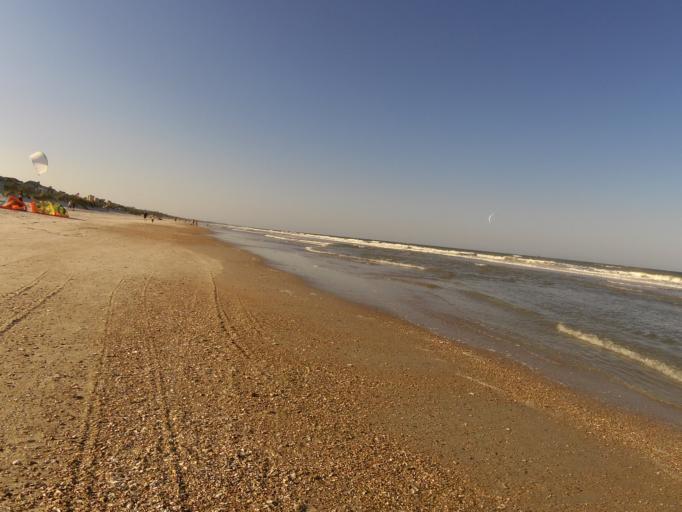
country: US
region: Florida
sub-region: Duval County
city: Atlantic Beach
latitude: 30.3479
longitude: -81.3967
